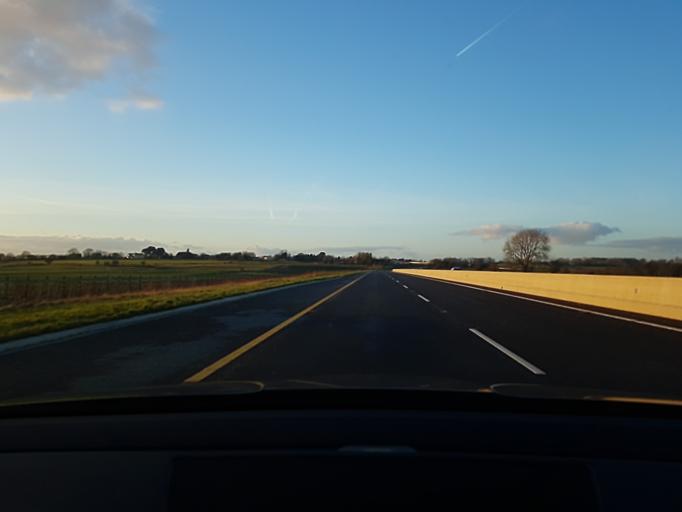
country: IE
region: Connaught
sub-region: County Galway
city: Tuam
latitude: 53.4298
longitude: -8.8387
